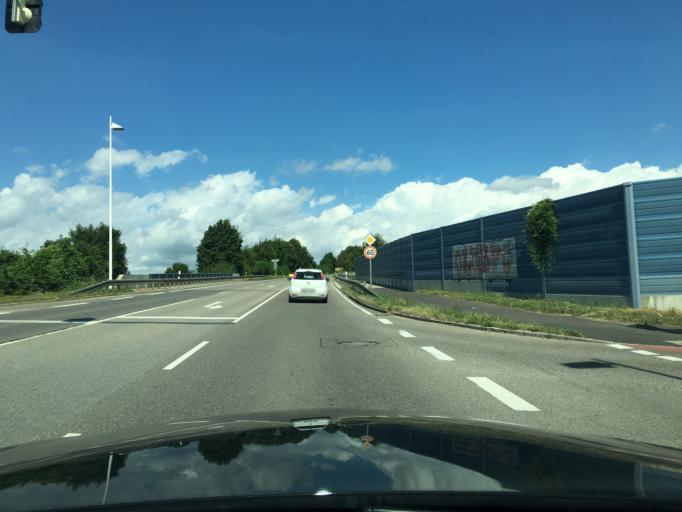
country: DE
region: Baden-Wuerttemberg
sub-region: Tuebingen Region
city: Dornstadt
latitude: 48.4145
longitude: 9.9370
